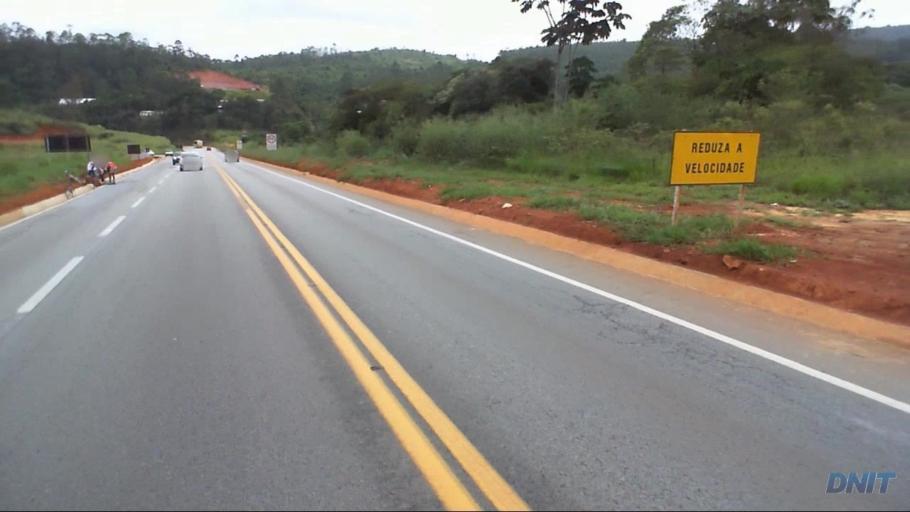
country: BR
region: Minas Gerais
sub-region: Joao Monlevade
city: Joao Monlevade
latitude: -19.8597
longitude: -43.1236
